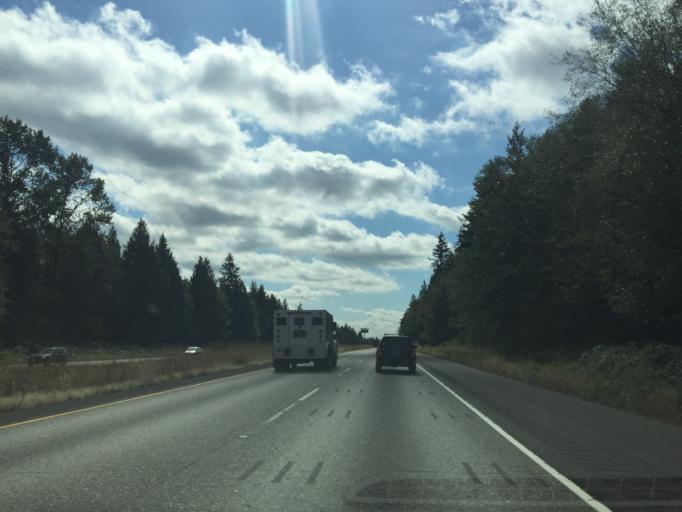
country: US
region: Washington
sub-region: Skagit County
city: Burlington
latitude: 48.5696
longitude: -122.3482
